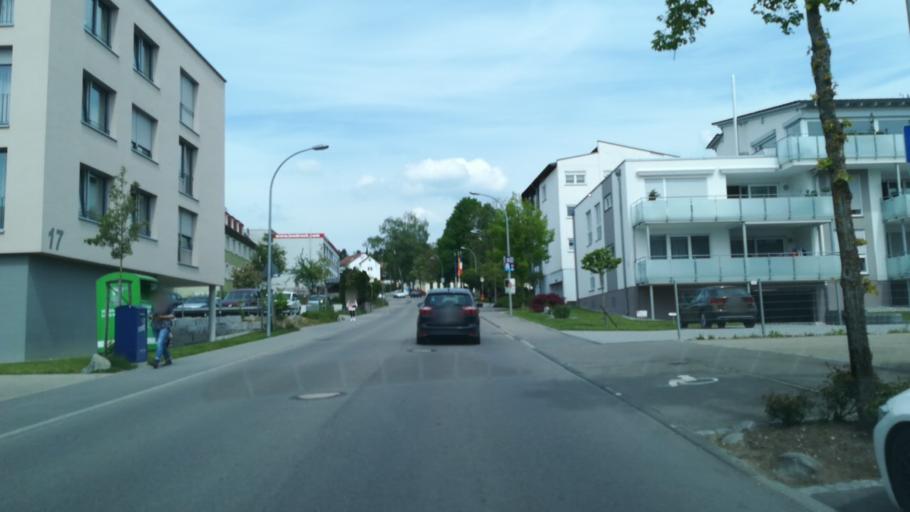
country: DE
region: Baden-Wuerttemberg
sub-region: Freiburg Region
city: Stockach
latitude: 47.8554
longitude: 9.0169
